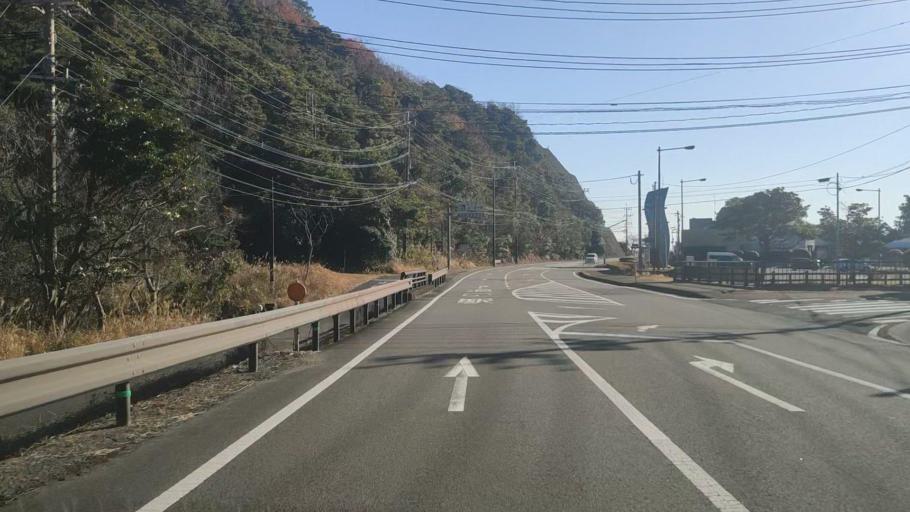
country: JP
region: Miyazaki
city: Nobeoka
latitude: 32.6856
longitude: 131.7995
